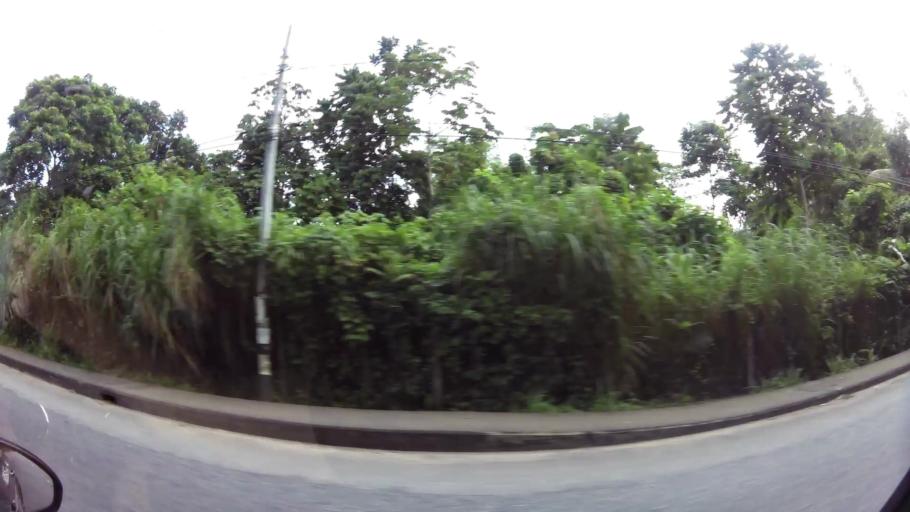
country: TT
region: San Juan/Laventille
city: Laventille
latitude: 10.7090
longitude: -61.4633
